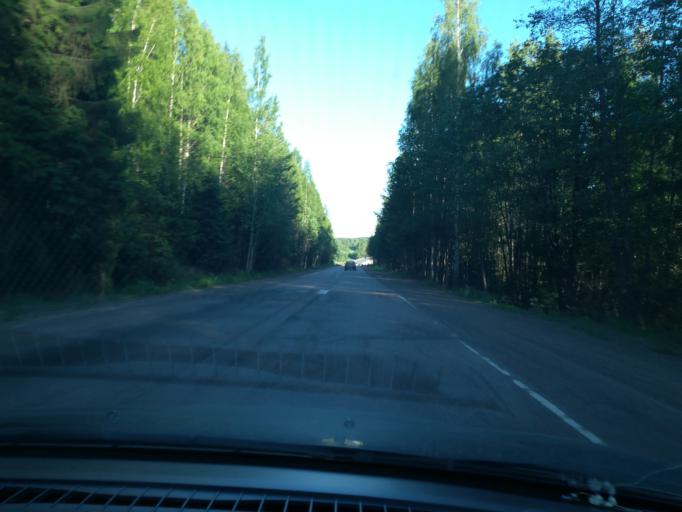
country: RU
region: Leningrad
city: Lesogorskiy
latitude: 61.0158
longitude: 28.9117
